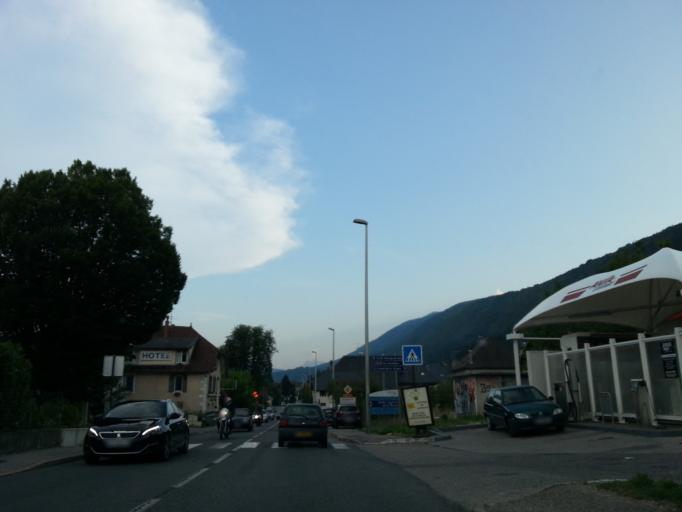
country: FR
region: Rhone-Alpes
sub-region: Departement de la Haute-Savoie
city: Sevrier
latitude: 45.8766
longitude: 6.1416
